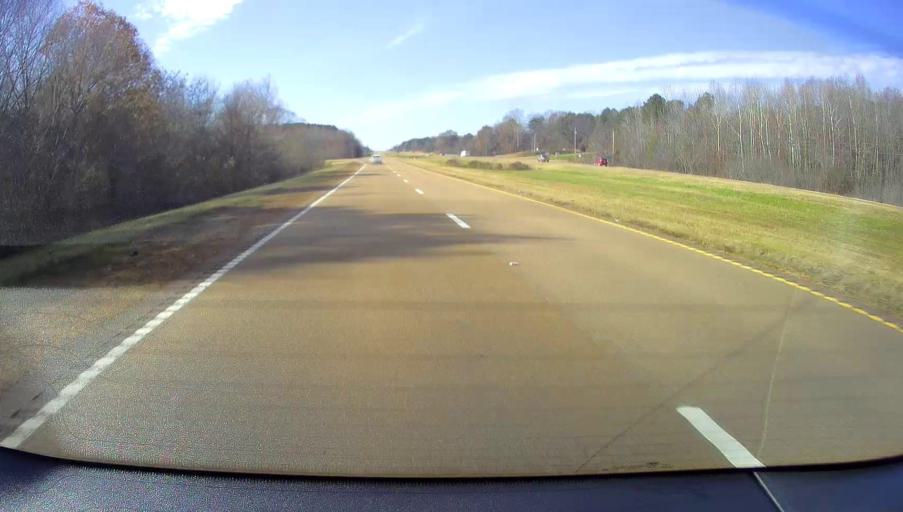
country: US
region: Mississippi
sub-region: Benton County
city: Ashland
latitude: 34.9522
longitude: -89.0567
